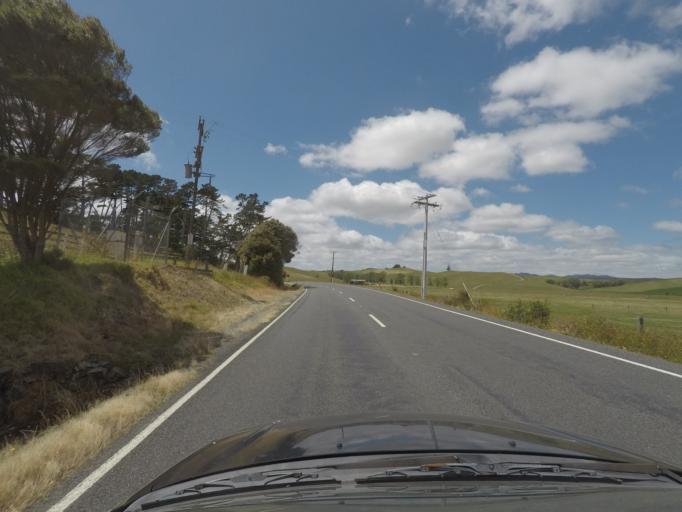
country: NZ
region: Northland
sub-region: Whangarei
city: Ruakaka
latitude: -35.9928
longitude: 174.4617
